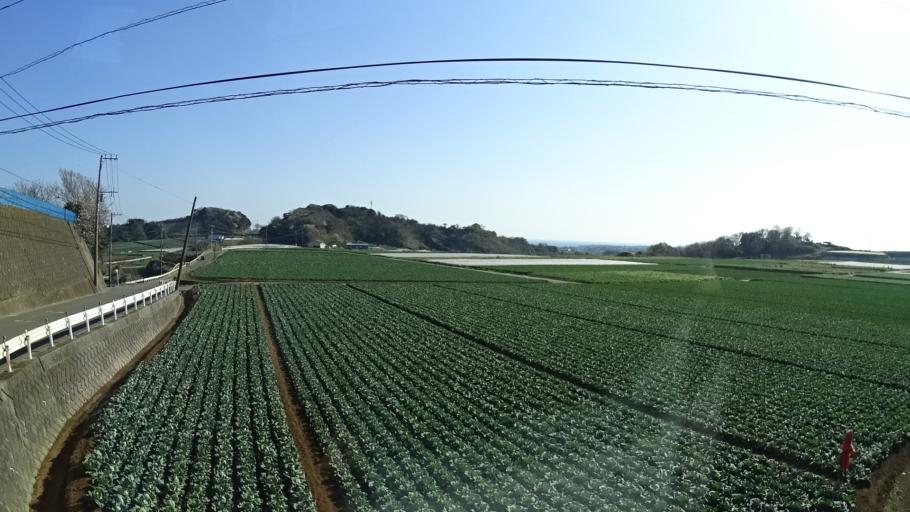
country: JP
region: Kanagawa
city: Miura
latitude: 35.1561
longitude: 139.6459
